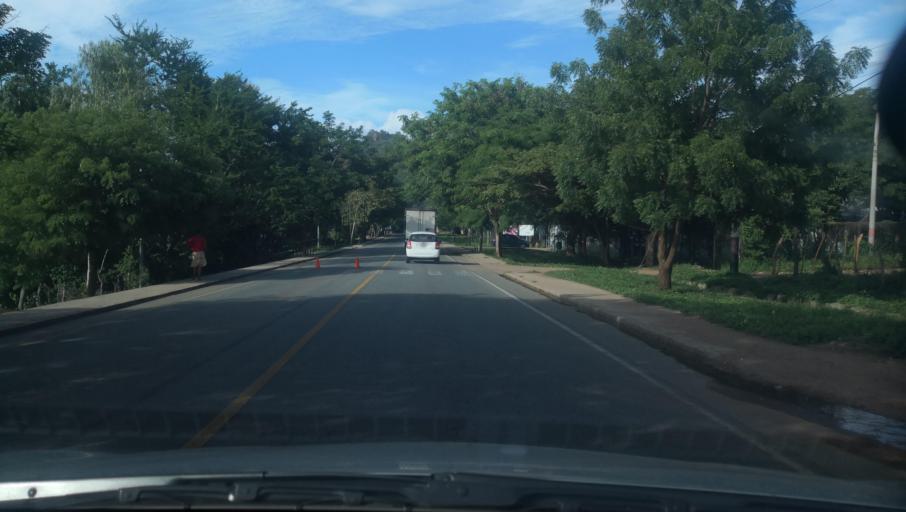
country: NI
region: Madriz
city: Totogalpa
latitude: 13.5613
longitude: -86.4907
